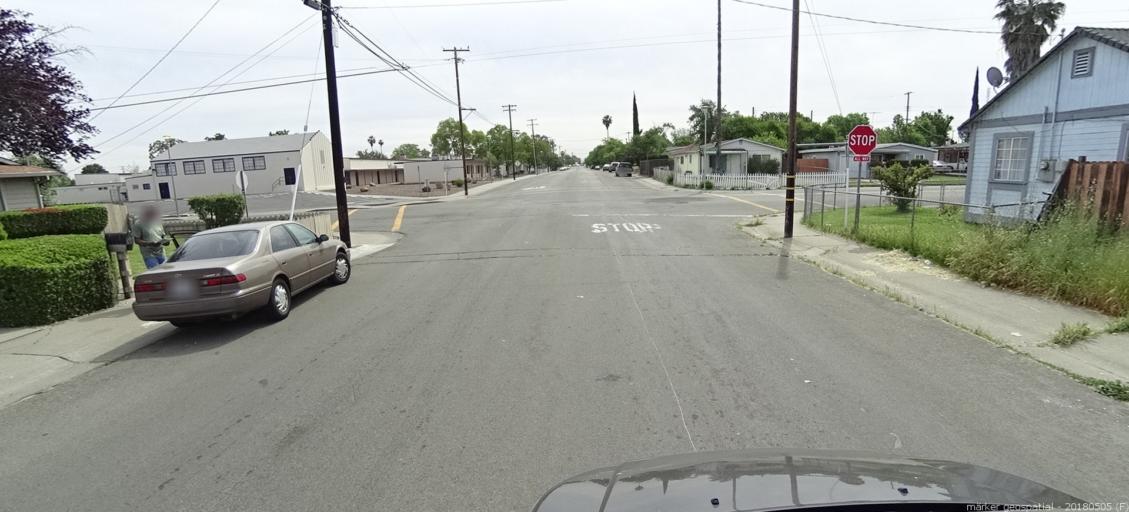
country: US
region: California
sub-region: Sacramento County
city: Rio Linda
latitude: 38.6402
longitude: -121.4389
